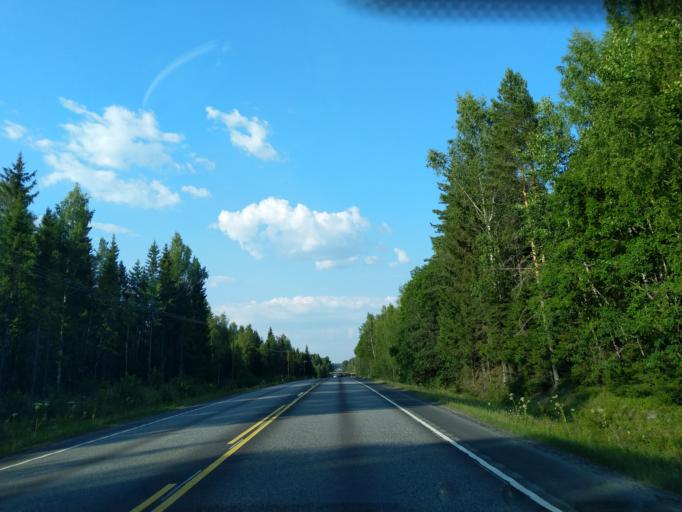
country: FI
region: Satakunta
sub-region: Pori
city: Pomarkku
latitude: 61.7234
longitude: 22.0585
